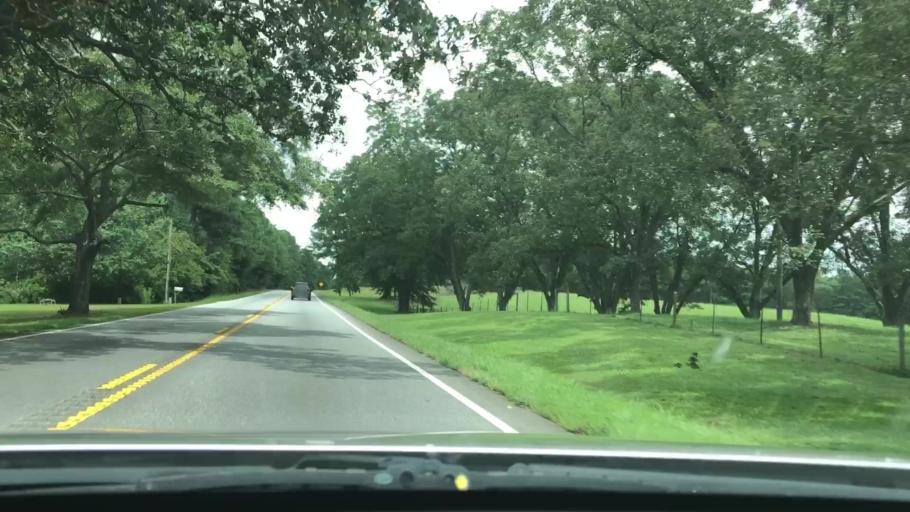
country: US
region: Georgia
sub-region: Lamar County
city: Barnesville
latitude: 33.1695
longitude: -84.0927
